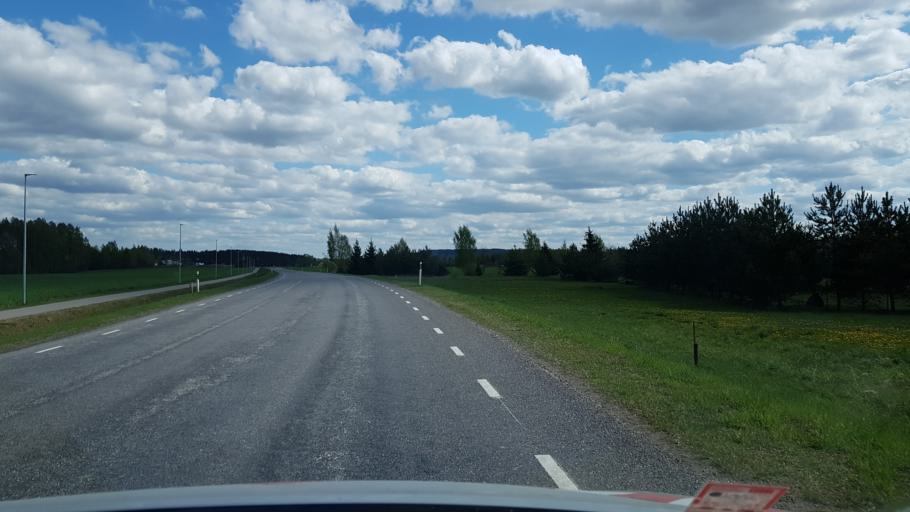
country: EE
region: Tartu
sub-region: UElenurme vald
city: Ulenurme
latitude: 58.3098
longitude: 26.8479
